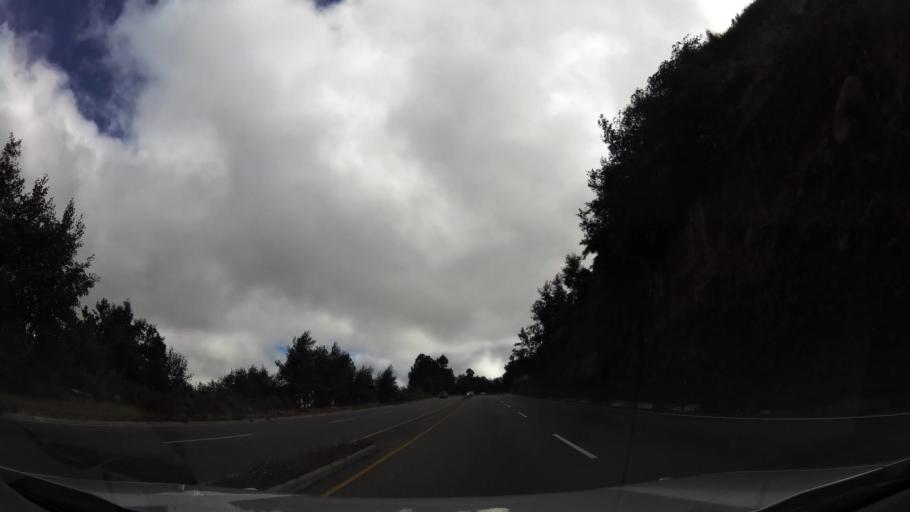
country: GT
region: Quetzaltenango
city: Salcaja
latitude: 14.8507
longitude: -91.4054
